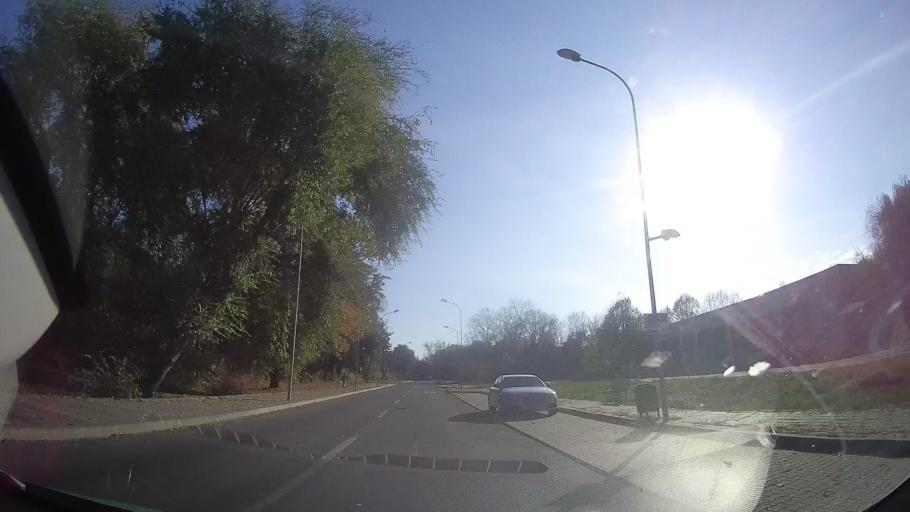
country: RO
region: Constanta
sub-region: Comuna Douazeci si Trei August
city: Douazeci si Trei August
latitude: 43.8618
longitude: 28.5980
